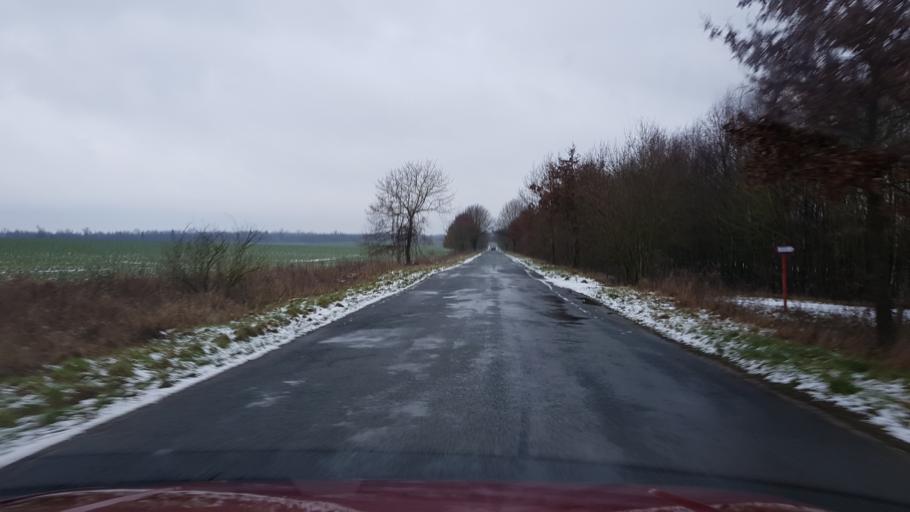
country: PL
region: West Pomeranian Voivodeship
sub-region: Powiat gryficki
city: Ploty
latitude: 53.6884
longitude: 15.2472
